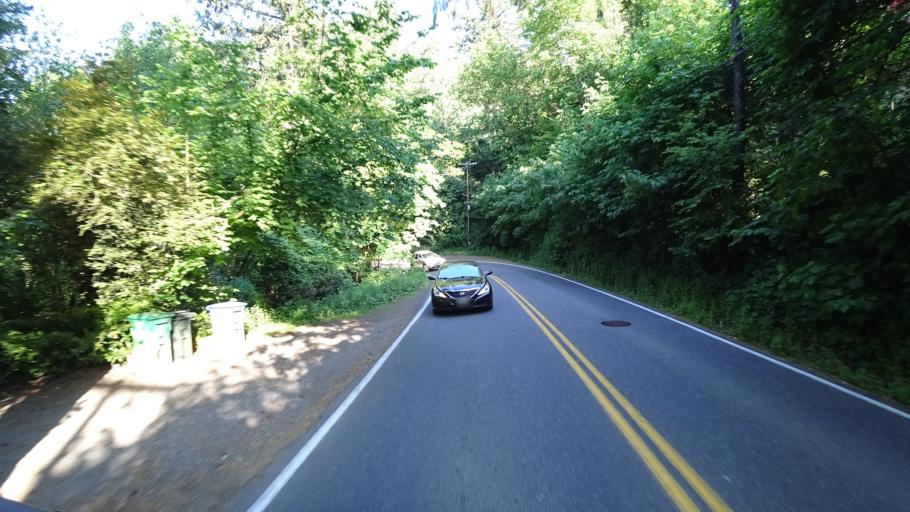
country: US
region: Oregon
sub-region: Washington County
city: West Slope
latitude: 45.5002
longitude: -122.7174
